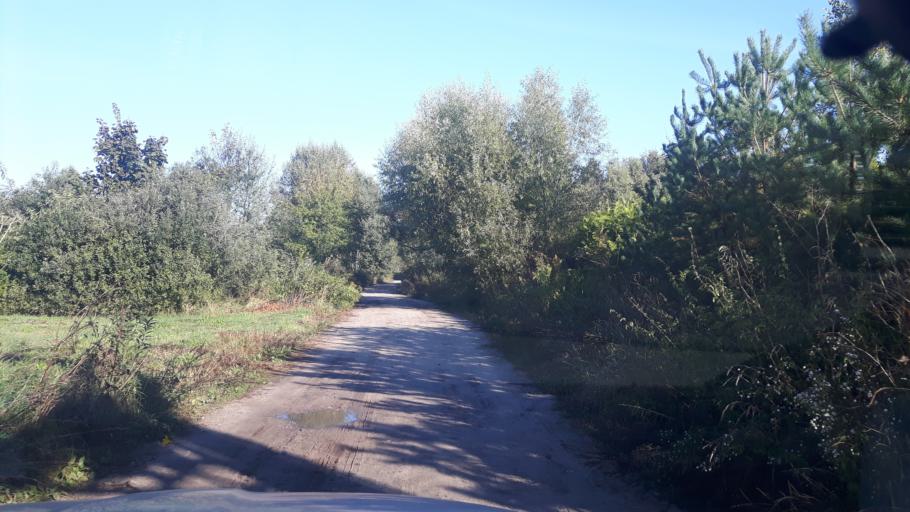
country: PL
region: Masovian Voivodeship
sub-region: Powiat legionowski
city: Stanislawow Pierwszy
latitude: 52.3634
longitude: 21.0378
